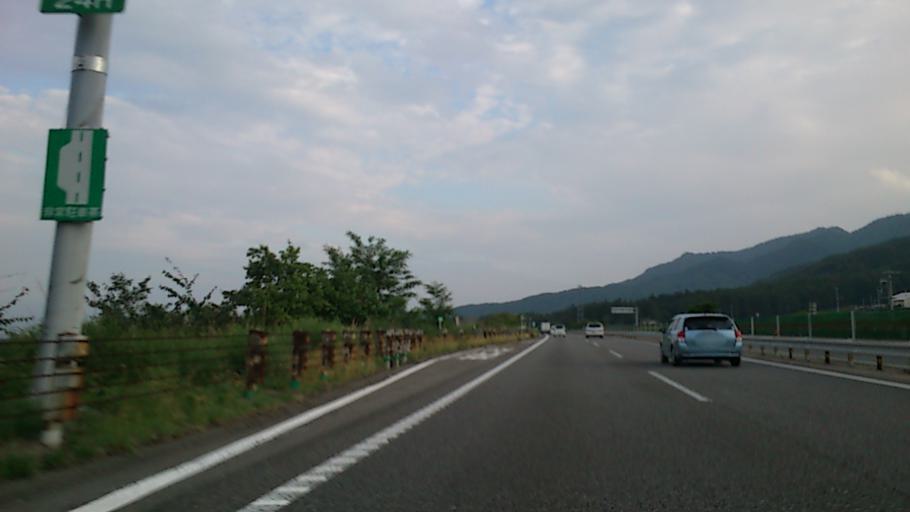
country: JP
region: Nagano
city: Ina
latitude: 35.7237
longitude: 137.9086
